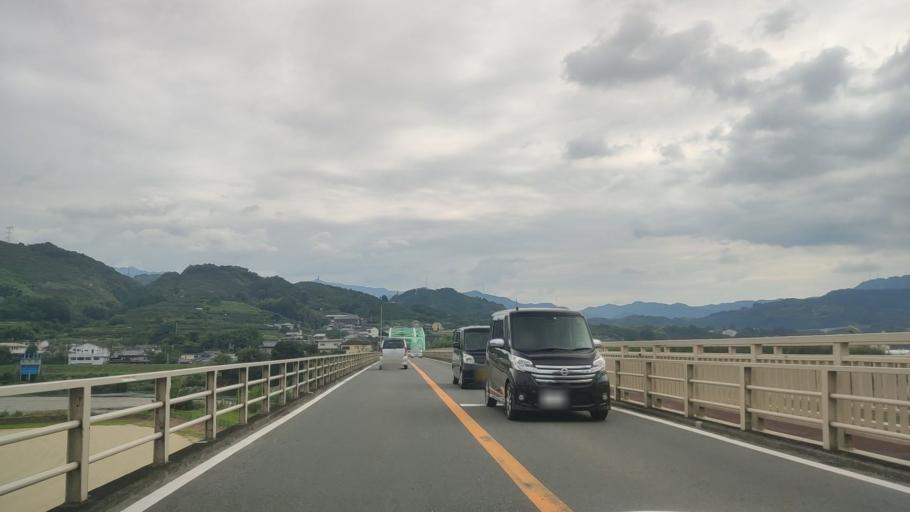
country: JP
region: Wakayama
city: Hashimoto
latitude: 34.3004
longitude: 135.5786
